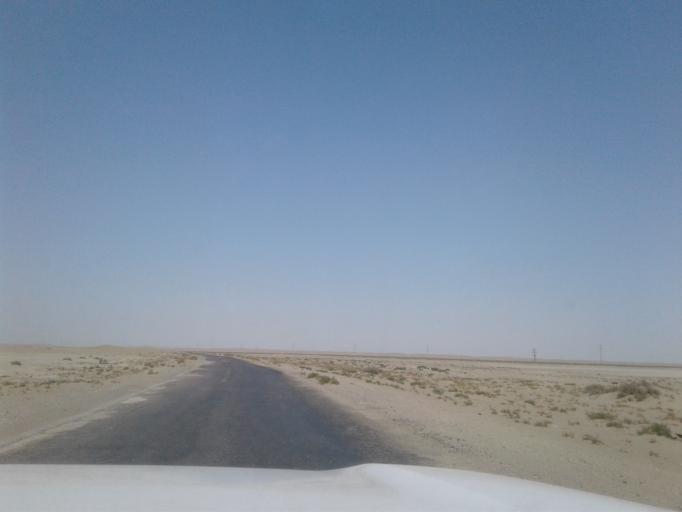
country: TM
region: Balkan
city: Gumdag
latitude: 38.3864
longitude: 54.3977
